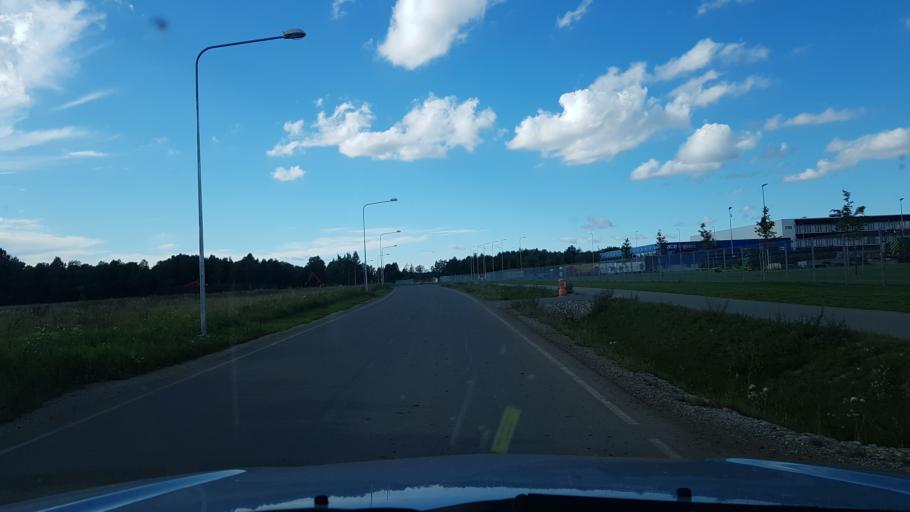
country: EE
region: Harju
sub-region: Rae vald
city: Jueri
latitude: 59.3621
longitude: 24.8643
